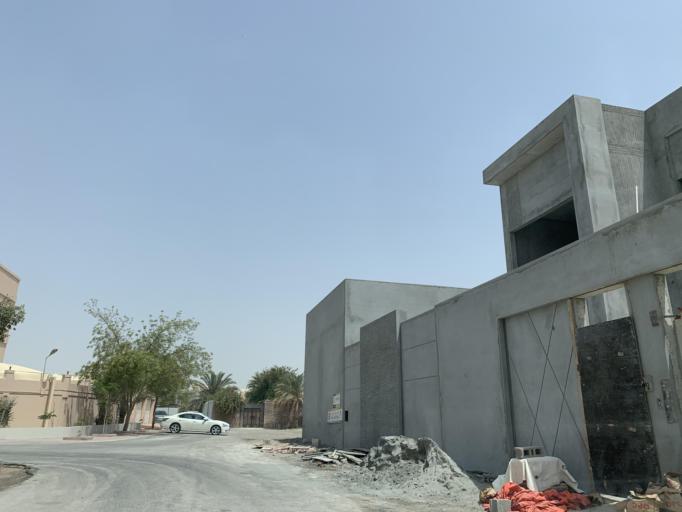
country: BH
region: Northern
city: Madinat `Isa
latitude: 26.1667
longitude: 50.5211
